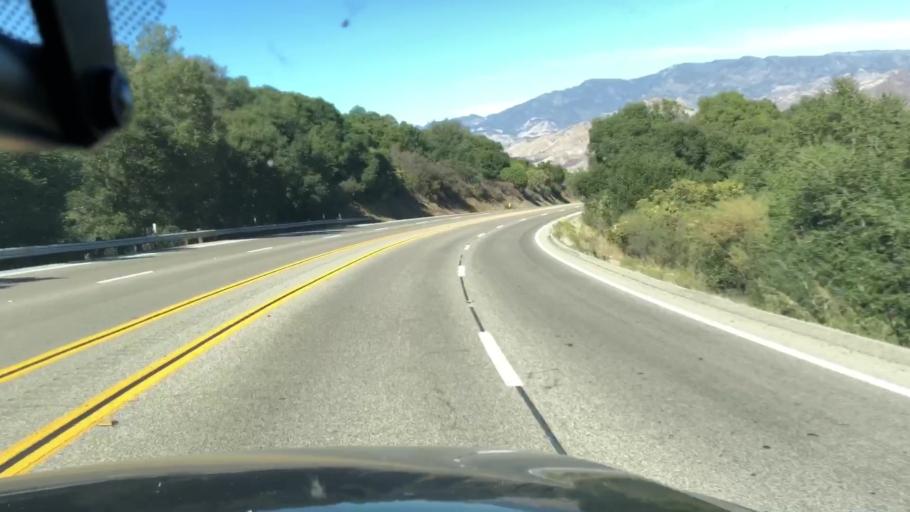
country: US
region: California
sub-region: Santa Barbara County
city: Goleta
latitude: 34.5168
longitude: -119.8291
